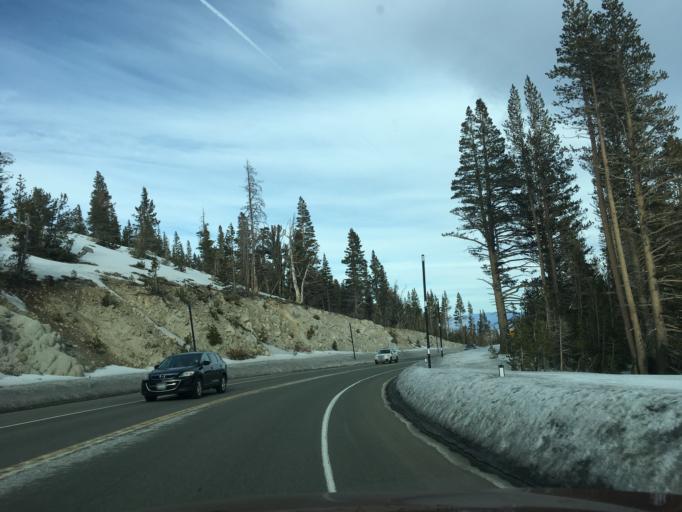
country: US
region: Nevada
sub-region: Washoe County
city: Incline Village
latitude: 39.3163
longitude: -119.9042
